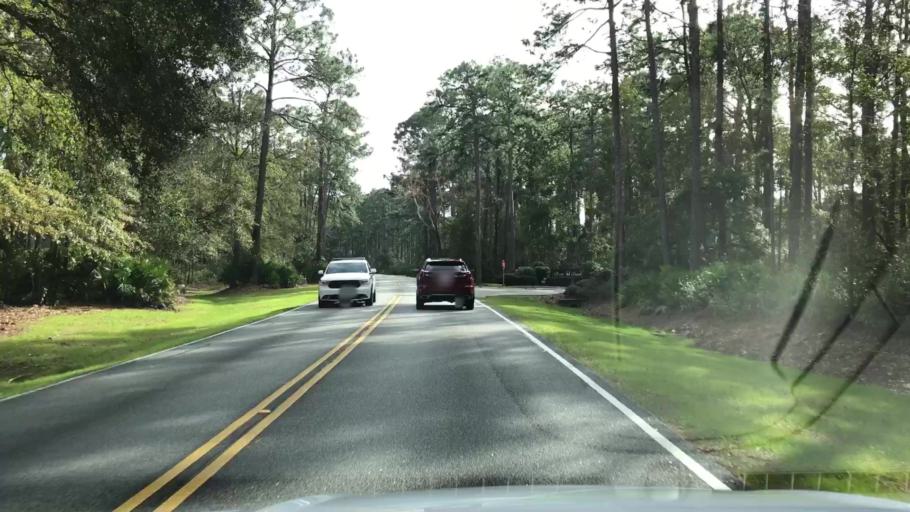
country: US
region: South Carolina
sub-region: Beaufort County
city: Hilton Head Island
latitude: 32.2315
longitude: -80.7252
